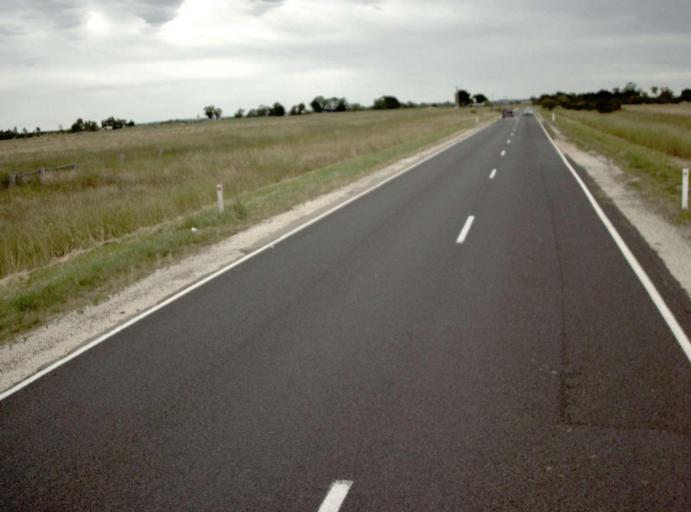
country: AU
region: Victoria
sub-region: Wellington
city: Sale
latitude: -38.0690
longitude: 147.1459
